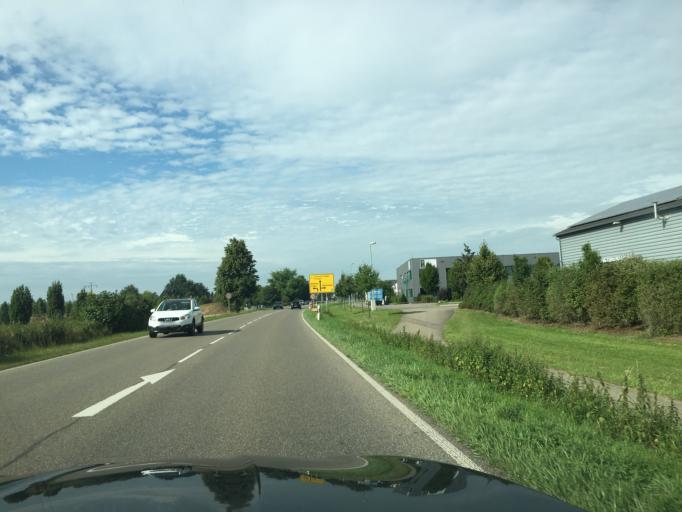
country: DE
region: Baden-Wuerttemberg
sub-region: Tuebingen Region
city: Oberdischingen
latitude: 48.3031
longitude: 9.8464
